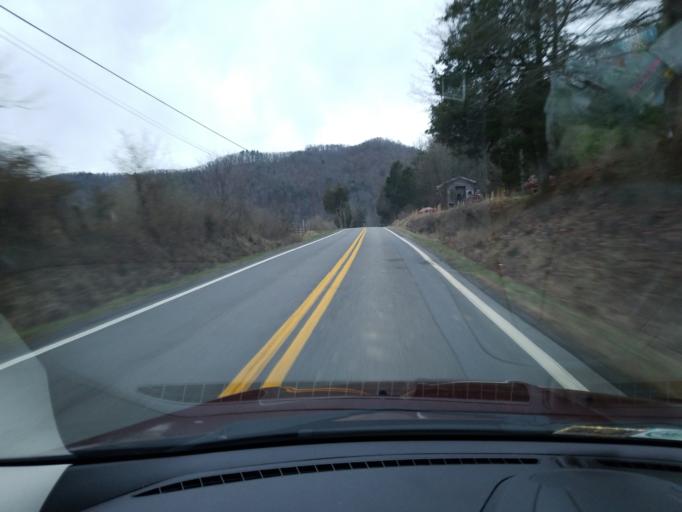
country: US
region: West Virginia
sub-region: Monroe County
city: Union
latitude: 37.5321
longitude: -80.6008
